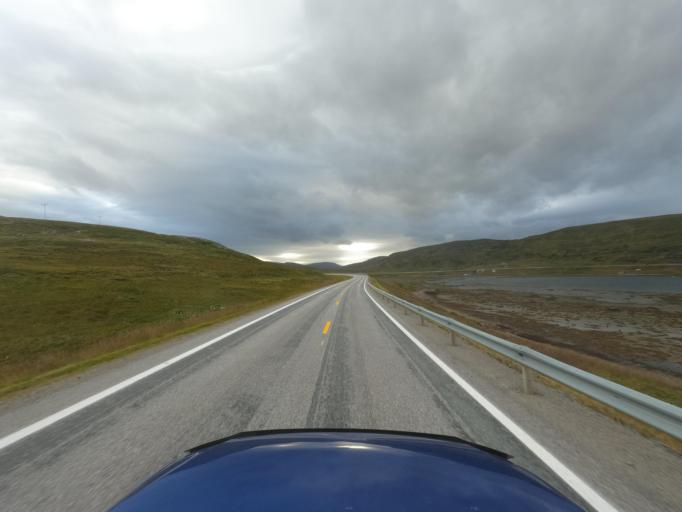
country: NO
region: Finnmark Fylke
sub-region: Nordkapp
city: Honningsvag
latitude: 70.8669
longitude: 25.7493
